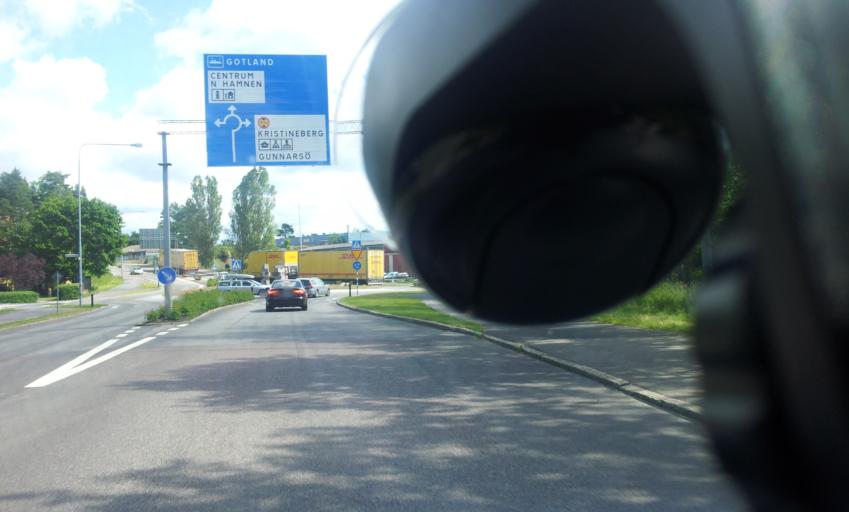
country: SE
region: Kalmar
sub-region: Oskarshamns Kommun
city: Oskarshamn
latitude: 57.2548
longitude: 16.4588
